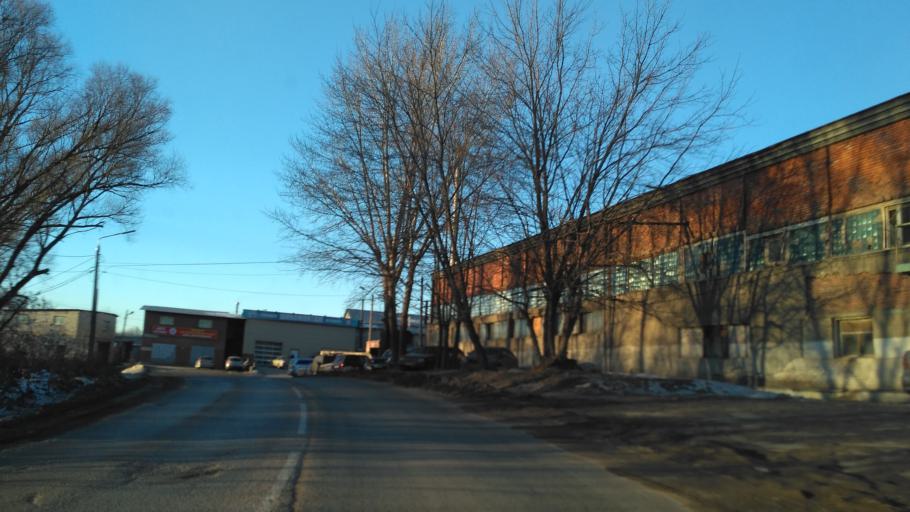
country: RU
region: Tula
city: Tula
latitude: 54.2226
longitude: 37.5897
